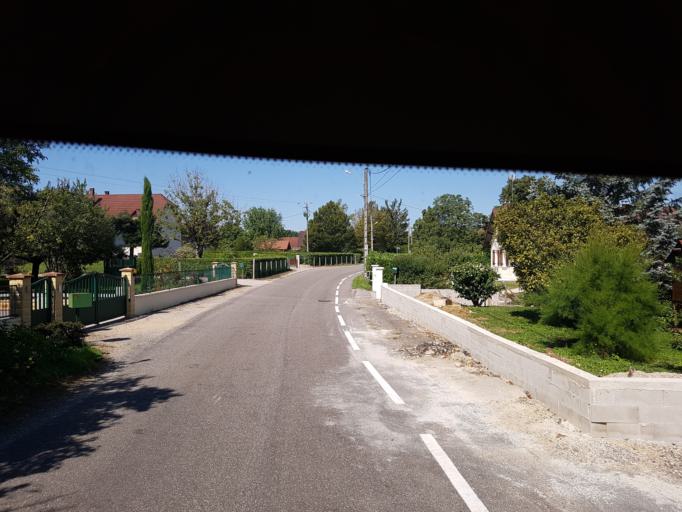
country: FR
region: Franche-Comte
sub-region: Departement du Jura
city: Perrigny
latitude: 46.7318
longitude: 5.5744
